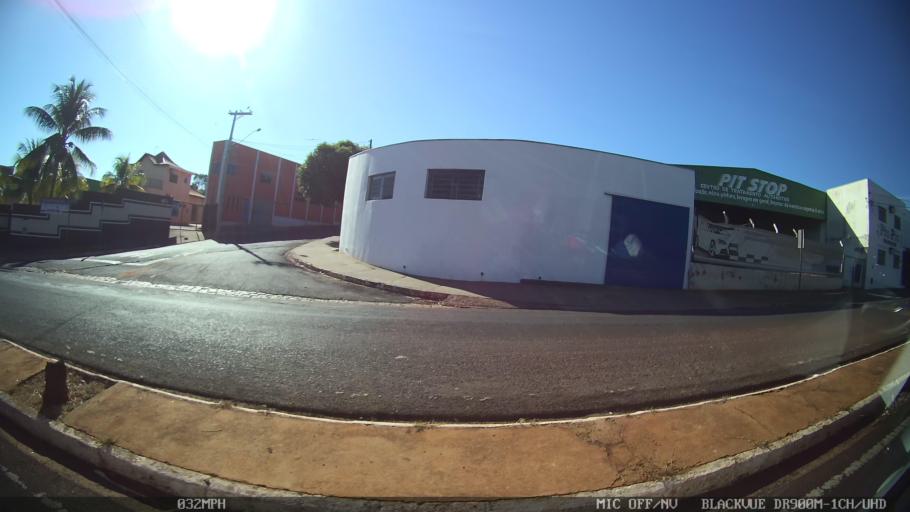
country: BR
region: Sao Paulo
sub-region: Olimpia
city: Olimpia
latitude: -20.7424
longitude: -48.8957
